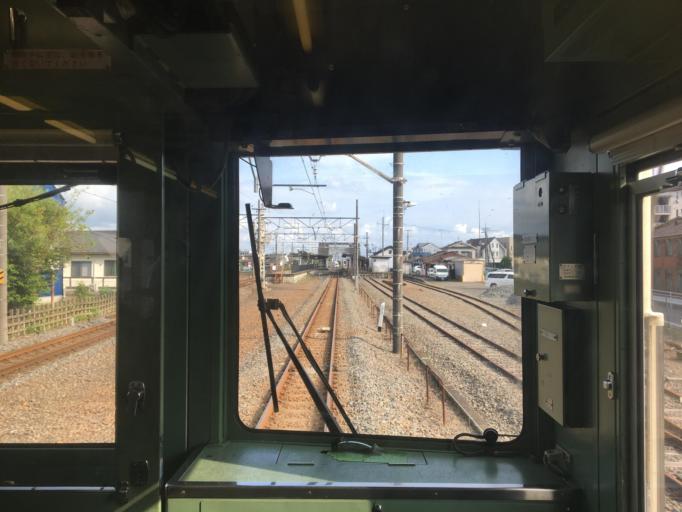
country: JP
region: Tochigi
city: Ashikaga
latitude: 36.3067
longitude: 139.4580
